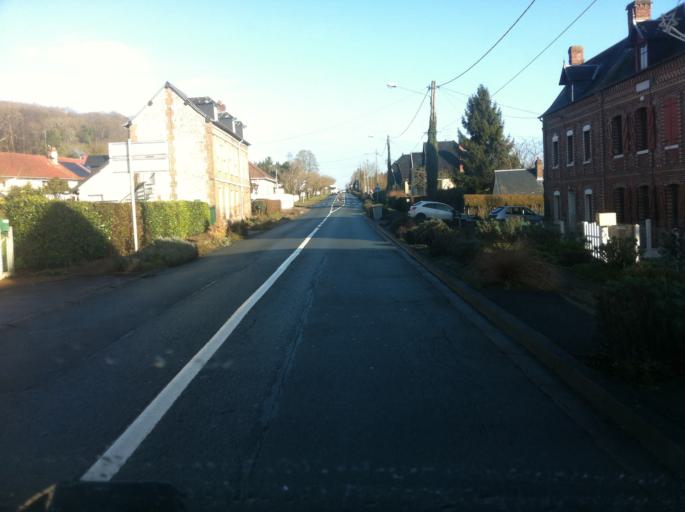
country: FR
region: Haute-Normandie
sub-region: Departement de la Seine-Maritime
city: Duclair
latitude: 49.4724
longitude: 0.8614
